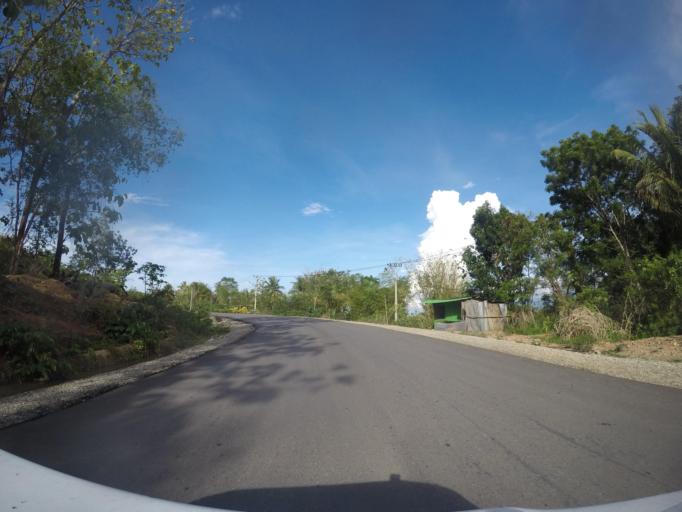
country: TL
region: Baucau
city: Baucau
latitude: -8.4960
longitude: 126.4543
